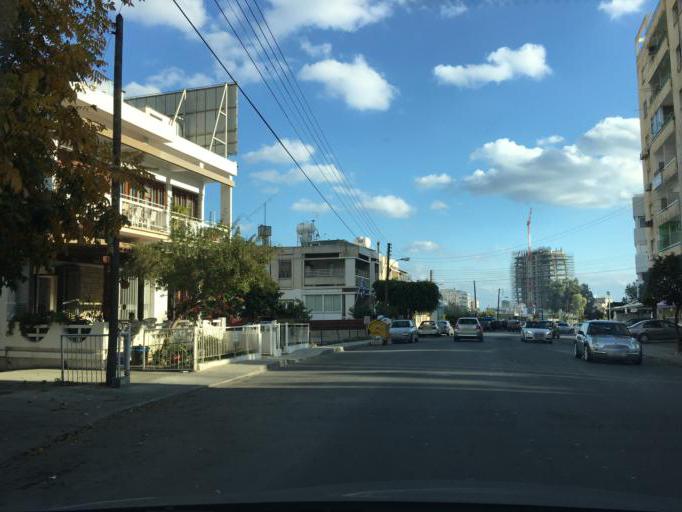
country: CY
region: Limassol
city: Limassol
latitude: 34.6934
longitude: 33.0667
